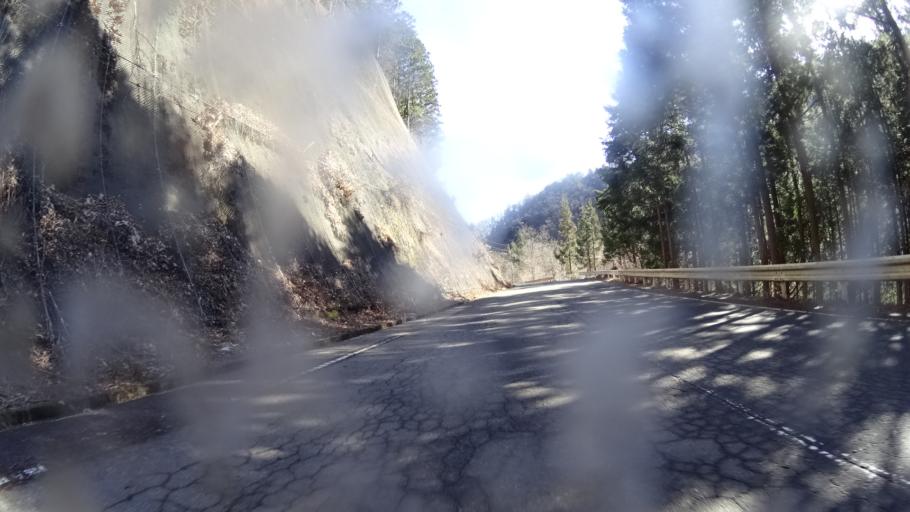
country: JP
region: Yamanashi
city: Otsuki
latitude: 35.7111
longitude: 138.9932
